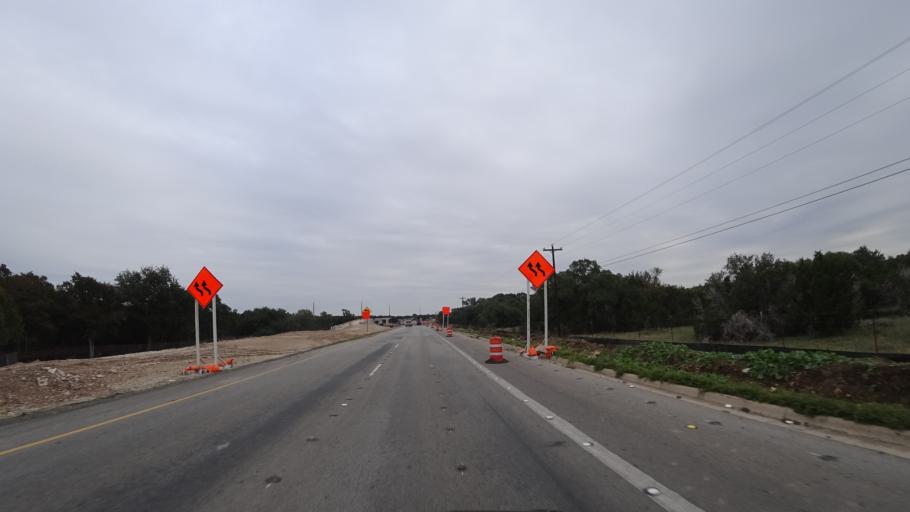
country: US
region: Texas
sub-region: Travis County
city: Shady Hollow
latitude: 30.1754
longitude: -97.8920
